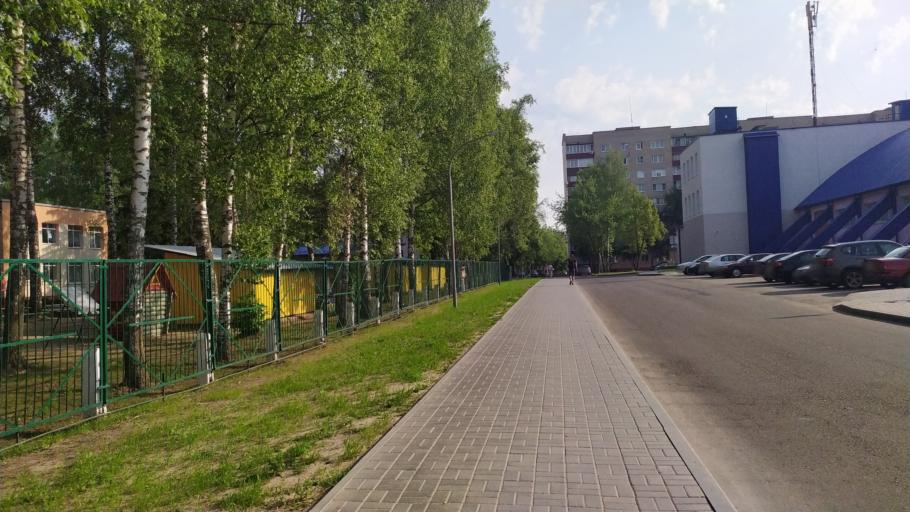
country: BY
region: Vitebsk
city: Navapolatsk
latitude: 55.5315
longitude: 28.6505
